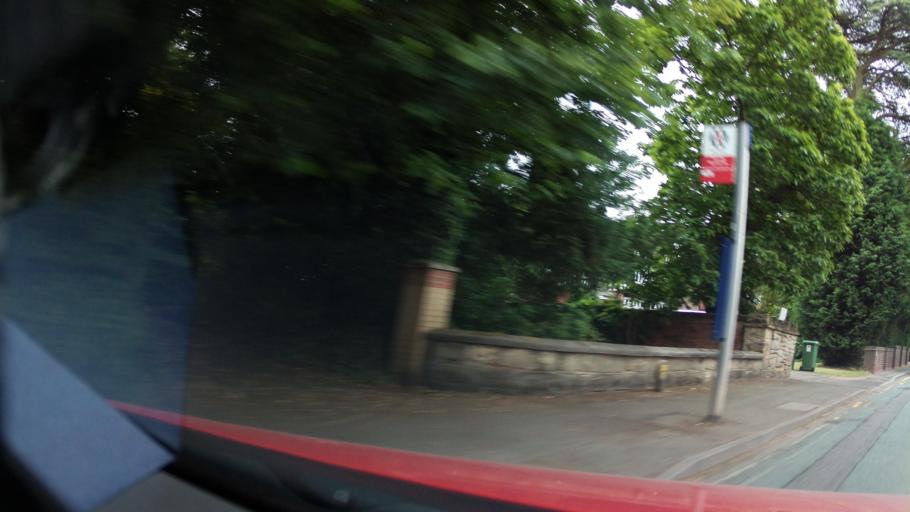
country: GB
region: England
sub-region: Wolverhampton
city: Wolverhampton
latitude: 52.5643
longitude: -2.1484
